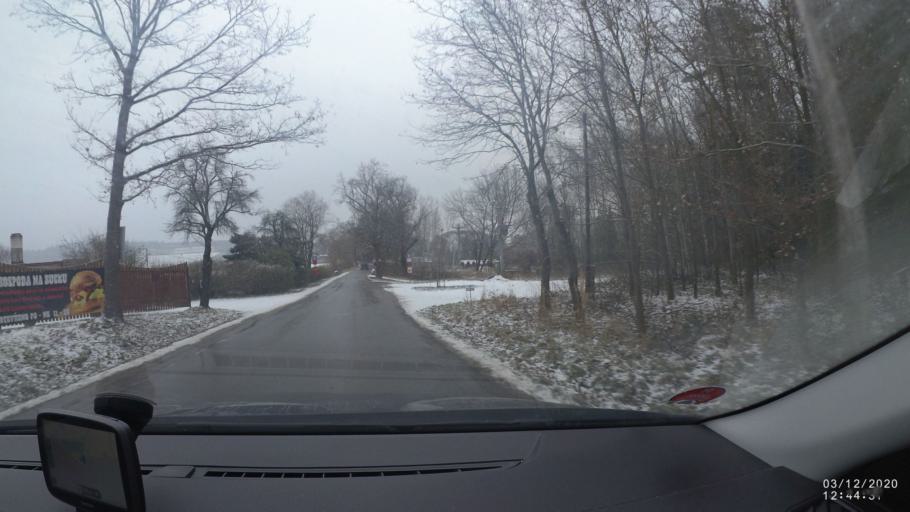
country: CZ
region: Central Bohemia
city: Revnicov
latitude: 50.1730
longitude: 13.8464
